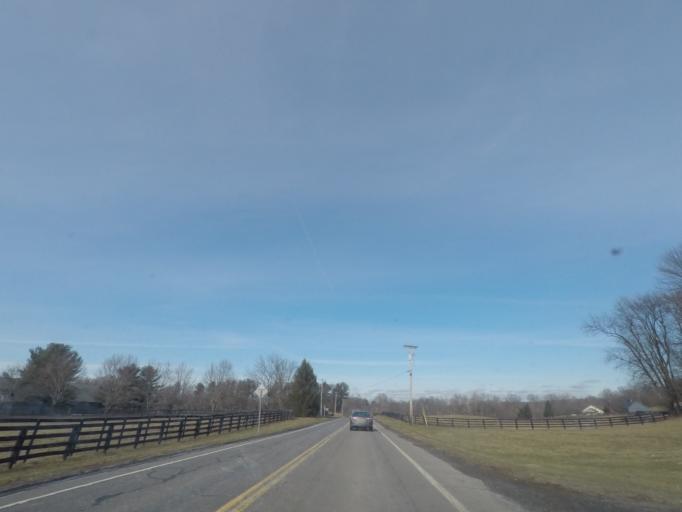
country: US
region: New York
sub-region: Columbia County
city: Niverville
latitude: 42.4577
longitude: -73.6450
